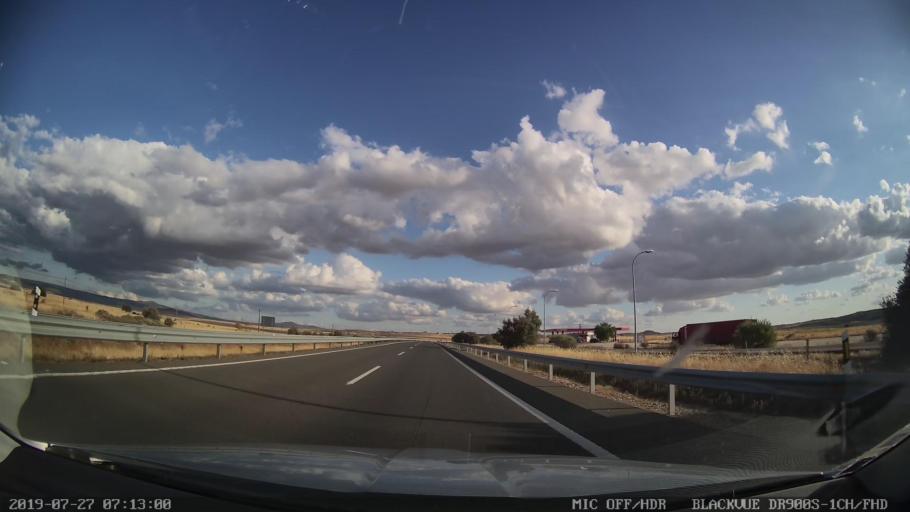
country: ES
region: Extremadura
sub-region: Provincia de Caceres
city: Trujillo
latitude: 39.5207
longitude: -5.8348
